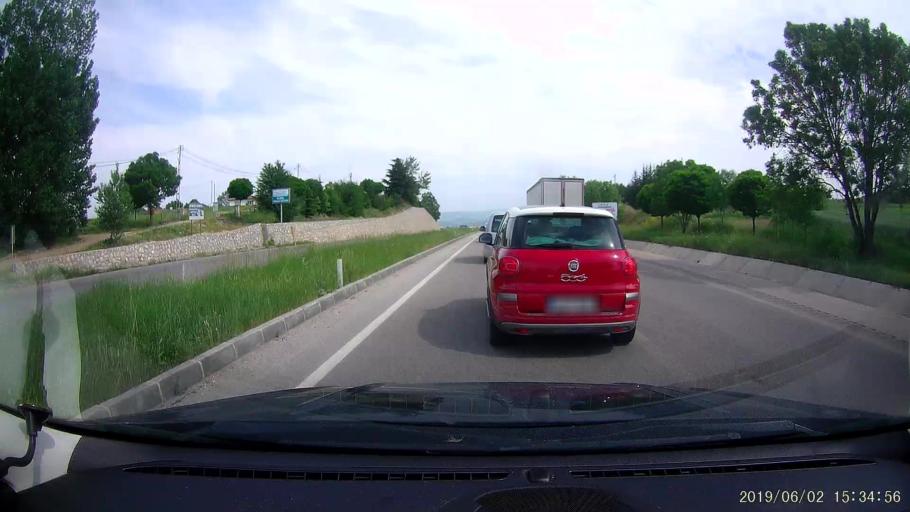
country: TR
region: Amasya
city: Gumushacikoy
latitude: 40.9055
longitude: 35.1788
